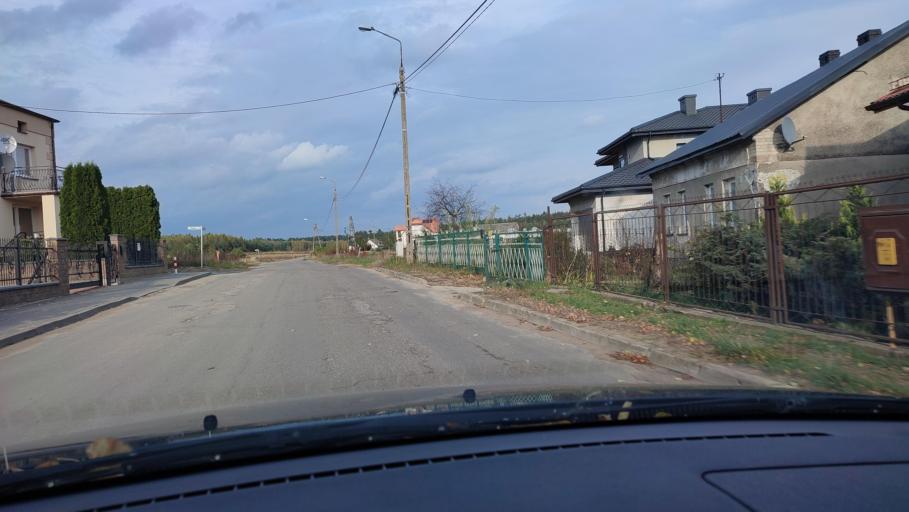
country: PL
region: Masovian Voivodeship
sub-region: Powiat mlawski
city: Mlawa
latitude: 53.1377
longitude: 20.3657
